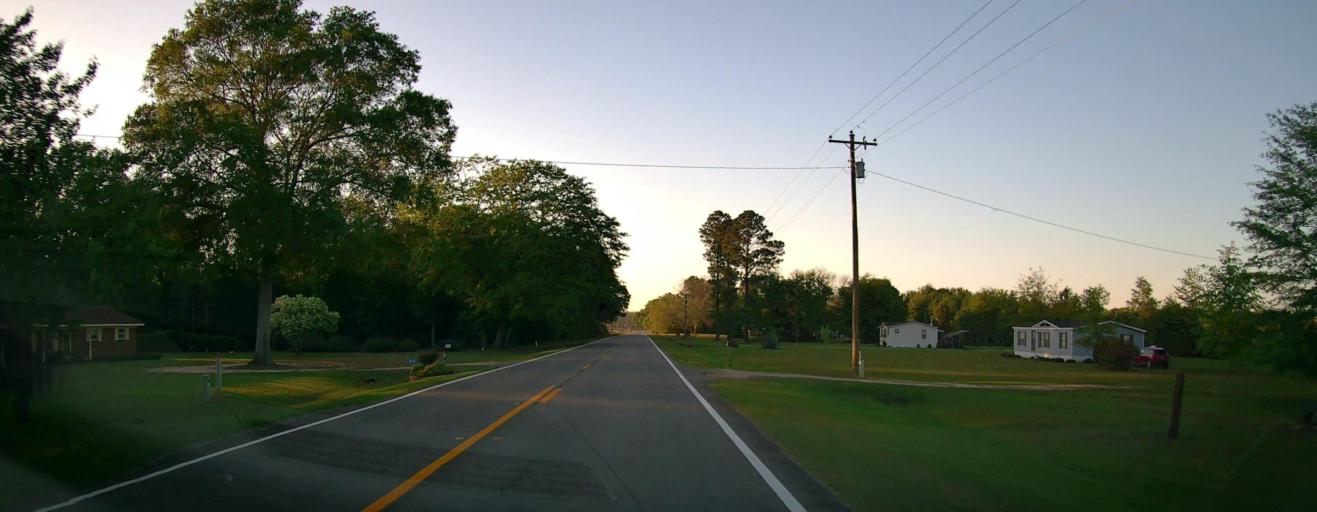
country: US
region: Georgia
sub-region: Irwin County
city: Ocilla
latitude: 31.6250
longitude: -83.2723
